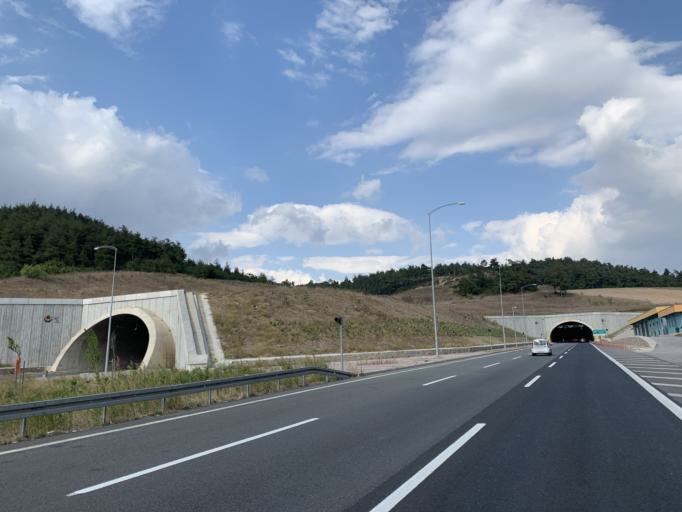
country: TR
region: Bursa
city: Demirtas
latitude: 40.3228
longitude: 29.0924
